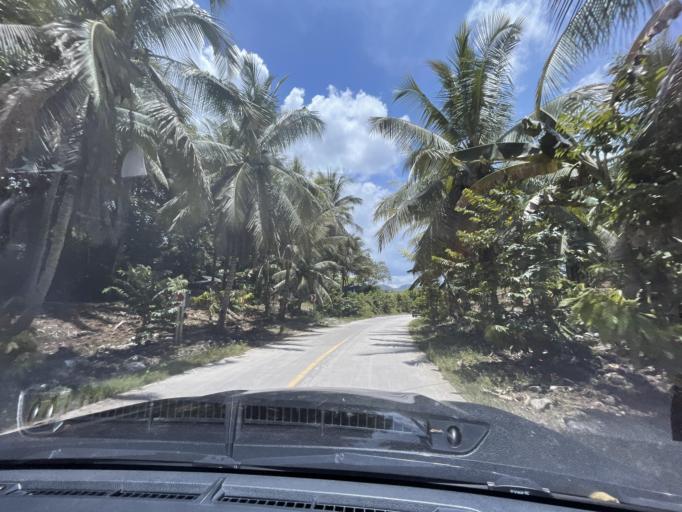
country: PH
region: Soccsksargen
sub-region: Province of Sarangani
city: Manga
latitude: 6.3839
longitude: 125.3164
